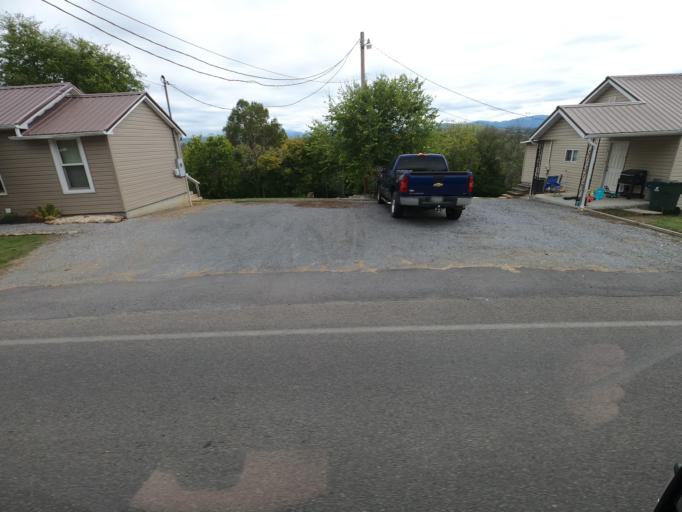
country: US
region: Tennessee
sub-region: Washington County
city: Jonesborough
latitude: 36.2551
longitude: -82.5414
